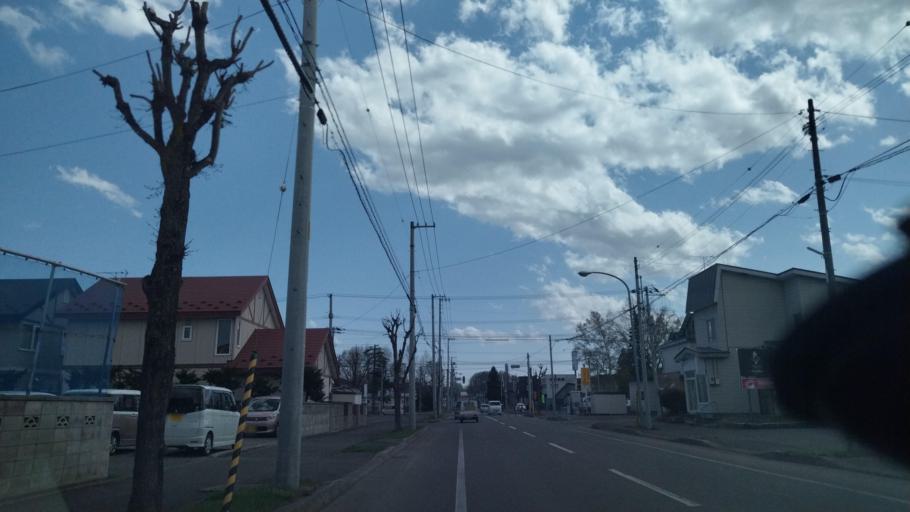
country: JP
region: Hokkaido
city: Obihiro
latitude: 42.9092
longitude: 143.1525
